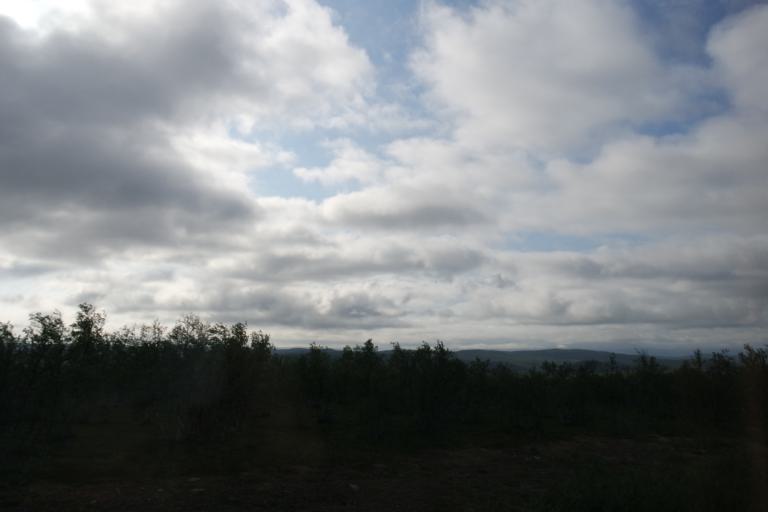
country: NO
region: Finnmark Fylke
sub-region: Karasjok
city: Karasjohka
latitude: 69.7205
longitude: 25.2376
